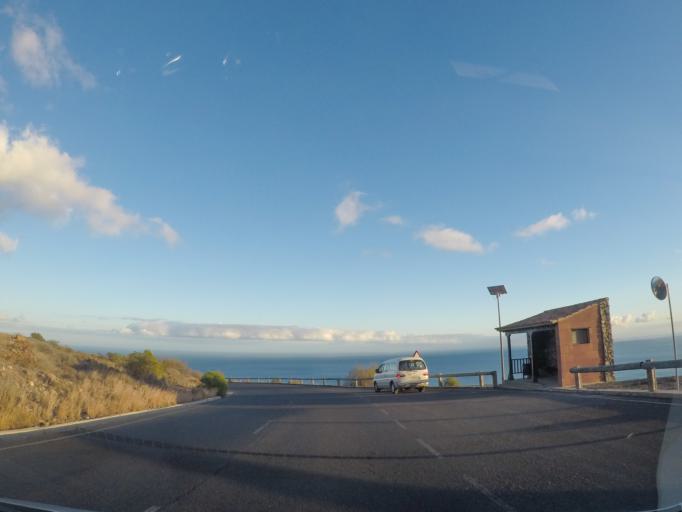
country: ES
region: Canary Islands
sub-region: Provincia de Santa Cruz de Tenerife
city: Alajero
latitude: 28.0379
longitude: -17.2251
